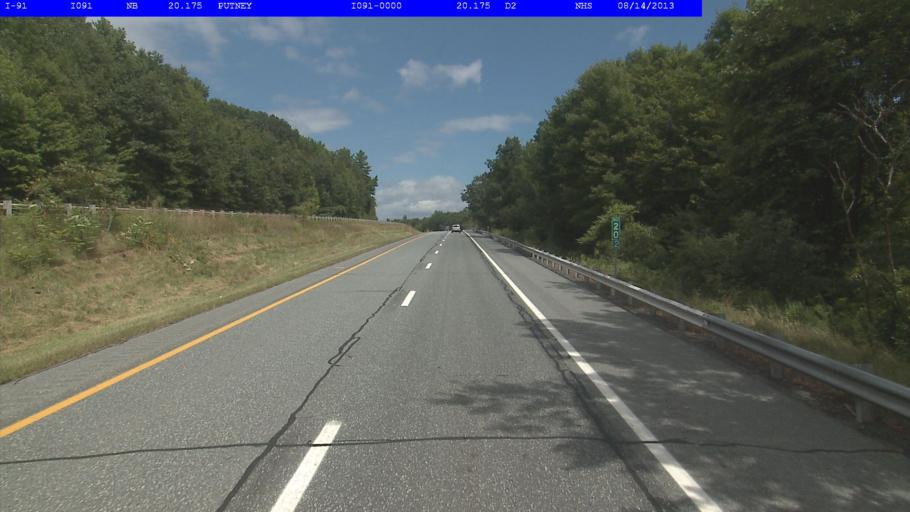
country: US
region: New Hampshire
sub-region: Cheshire County
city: Westmoreland
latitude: 42.9753
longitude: -72.4852
